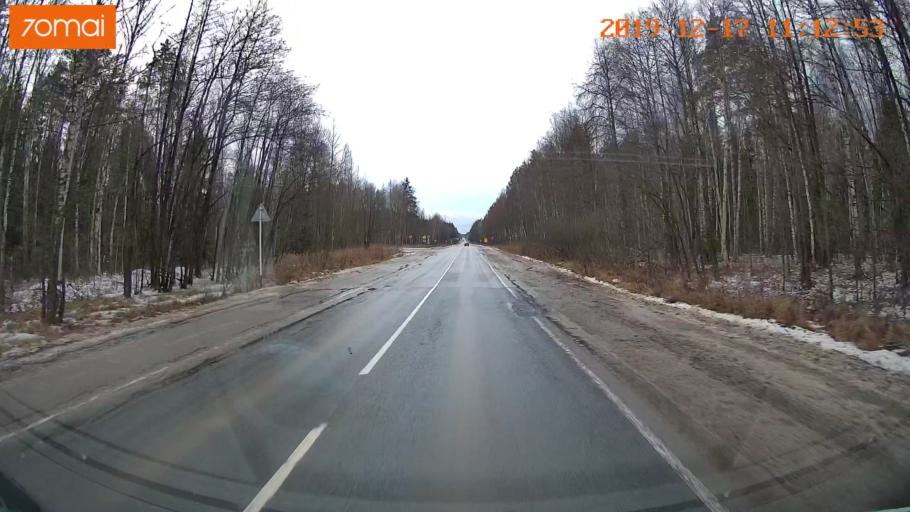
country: RU
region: Vladimir
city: Gus'-Khrustal'nyy
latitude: 55.5702
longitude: 40.6241
